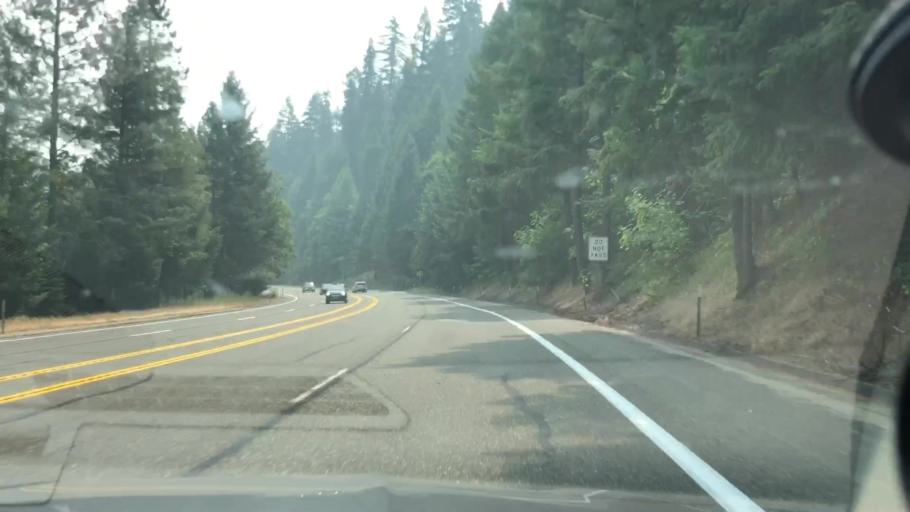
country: US
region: California
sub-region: El Dorado County
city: Pollock Pines
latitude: 38.7718
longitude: -120.4579
